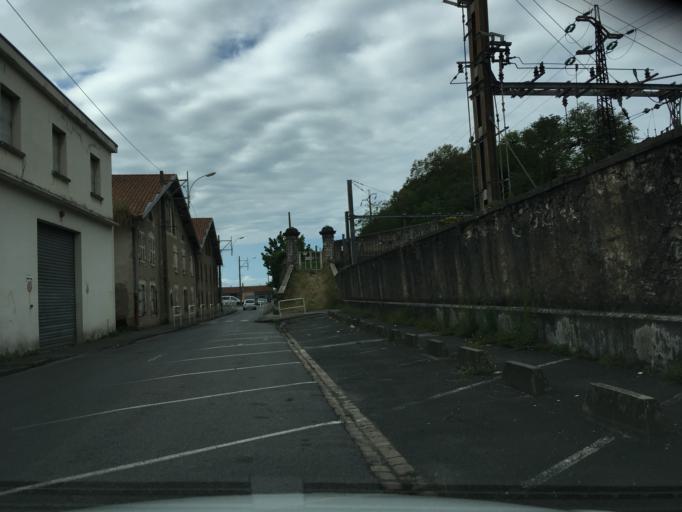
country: FR
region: Aquitaine
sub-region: Departement des Pyrenees-Atlantiques
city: Bayonne
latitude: 43.4967
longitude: -1.4731
